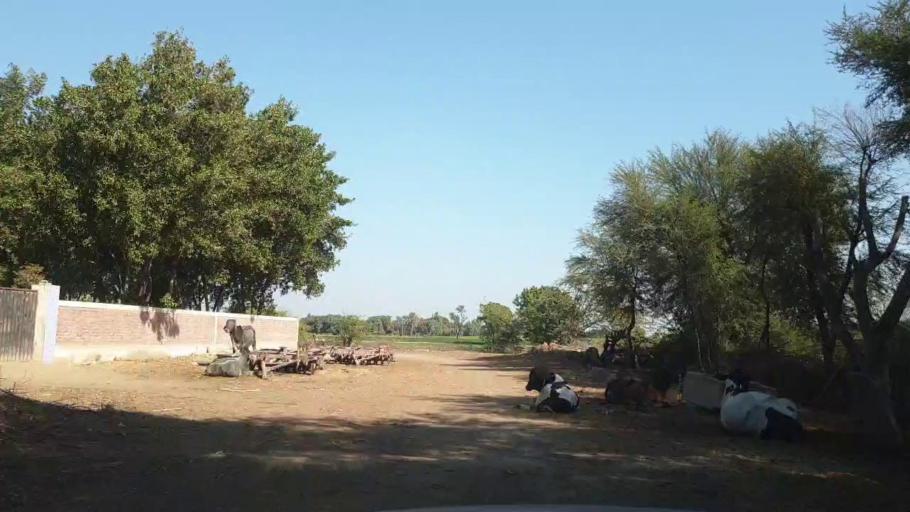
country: PK
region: Sindh
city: Tando Adam
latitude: 25.6452
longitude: 68.6859
